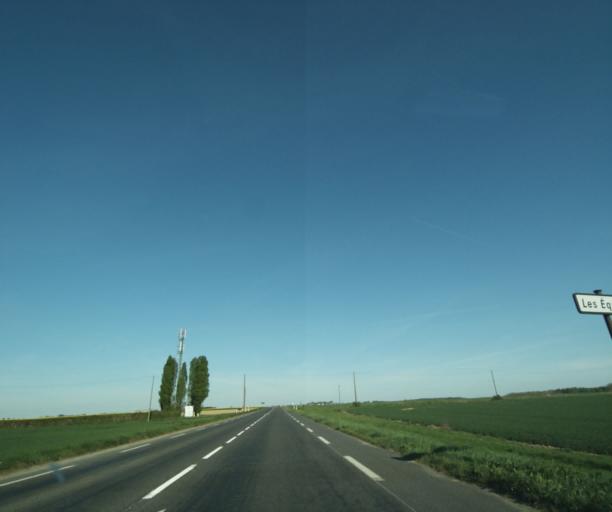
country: FR
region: Ile-de-France
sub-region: Departement de Seine-et-Marne
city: Bailly-Carrois
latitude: 48.5563
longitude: 2.9759
